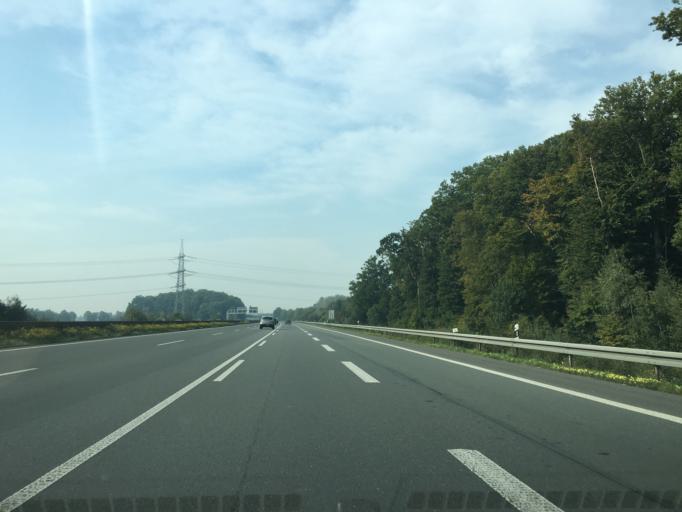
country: DE
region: North Rhine-Westphalia
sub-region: Regierungsbezirk Munster
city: Senden
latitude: 51.9148
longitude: 7.5509
